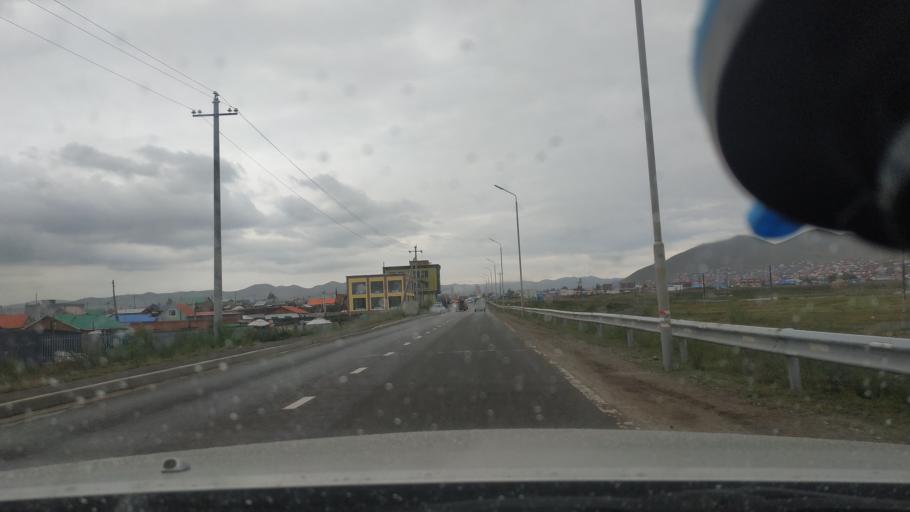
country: MN
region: Ulaanbaatar
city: Ulaanbaatar
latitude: 47.9035
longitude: 107.0354
